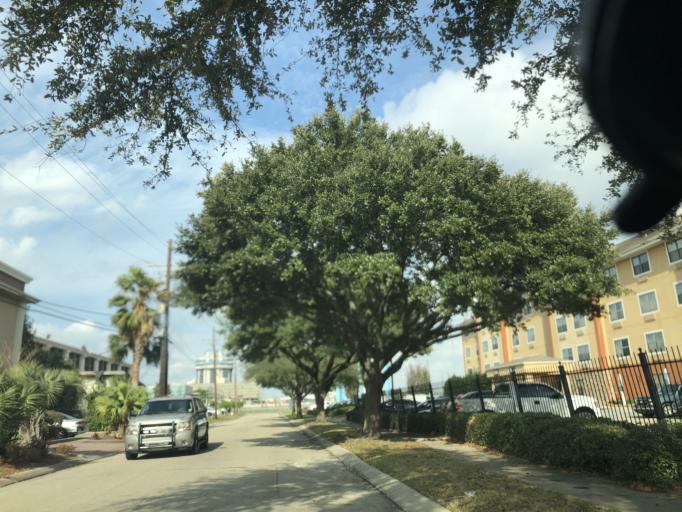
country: US
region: Louisiana
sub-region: Jefferson Parish
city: Metairie
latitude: 29.9951
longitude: -90.1585
